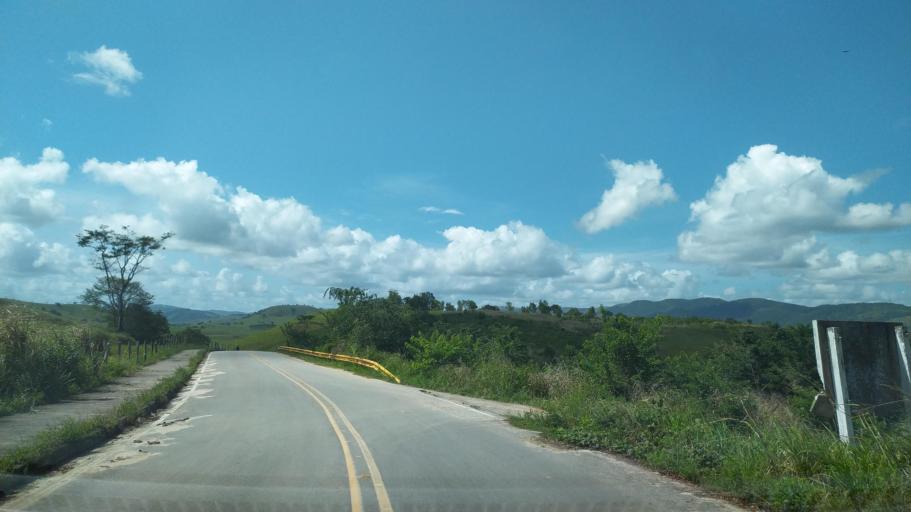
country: BR
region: Alagoas
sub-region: Uniao Dos Palmares
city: Uniao dos Palmares
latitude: -9.1685
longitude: -36.0592
